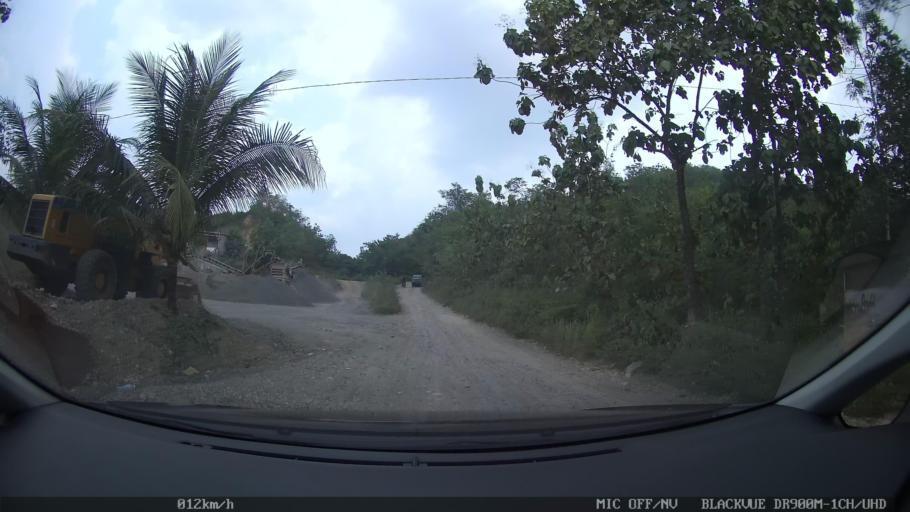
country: ID
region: Lampung
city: Gadingrejo
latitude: -5.3856
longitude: 105.0349
